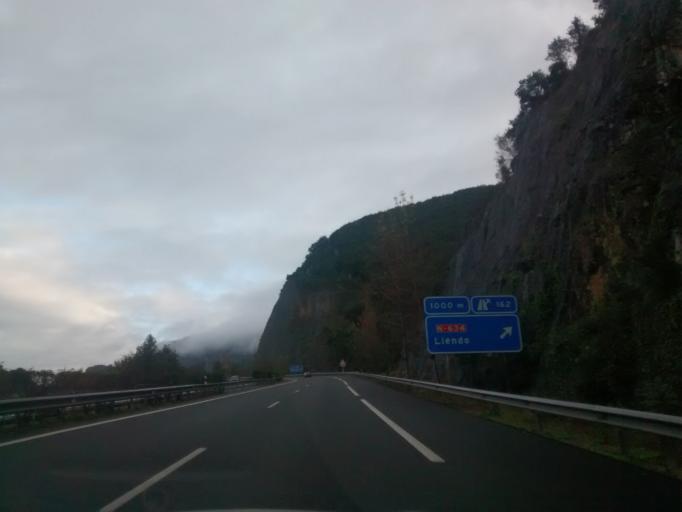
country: ES
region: Cantabria
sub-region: Provincia de Cantabria
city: Liendo
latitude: 43.3841
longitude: -3.3644
